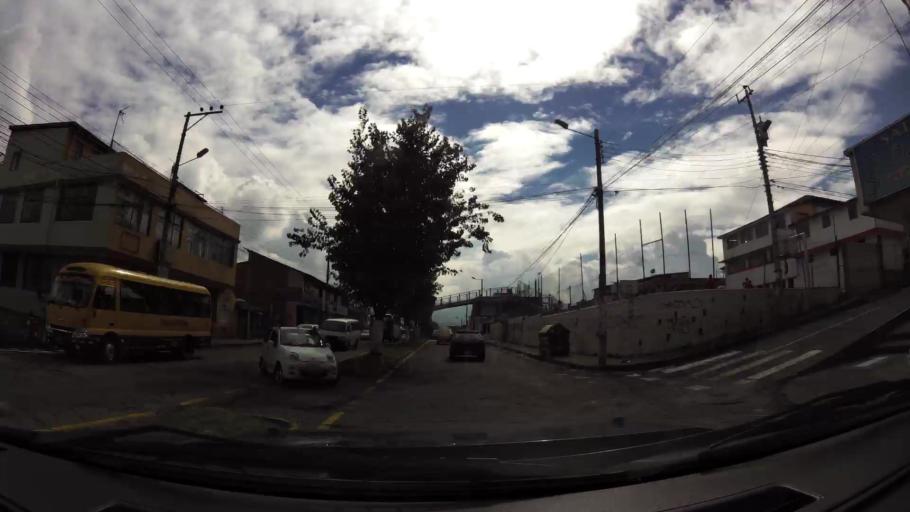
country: EC
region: Pichincha
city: Sangolqui
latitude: -0.3313
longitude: -78.4488
